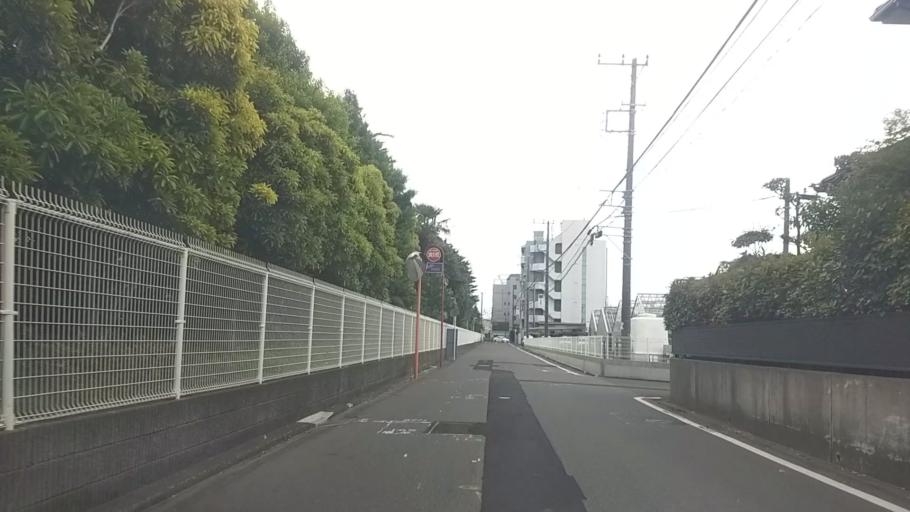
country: JP
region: Kanagawa
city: Fujisawa
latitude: 35.3395
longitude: 139.4734
